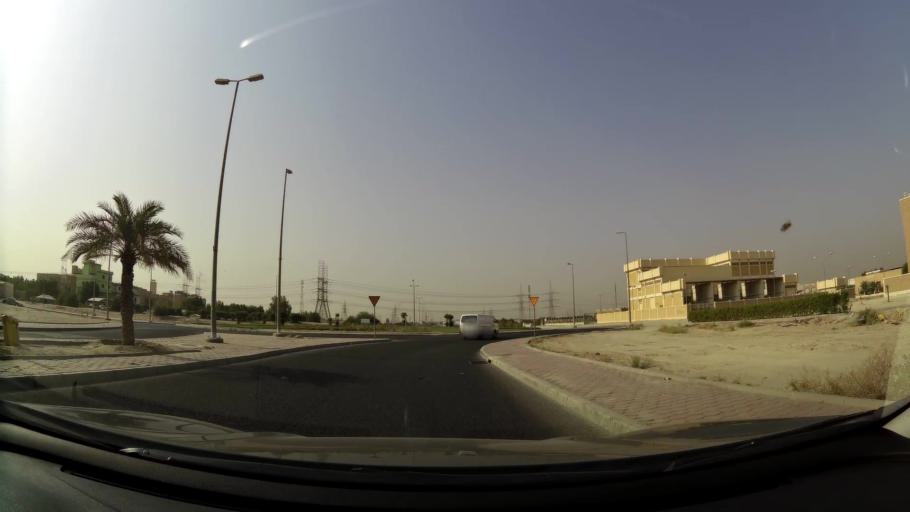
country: KW
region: Al Asimah
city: Ar Rabiyah
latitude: 29.2993
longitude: 47.8568
